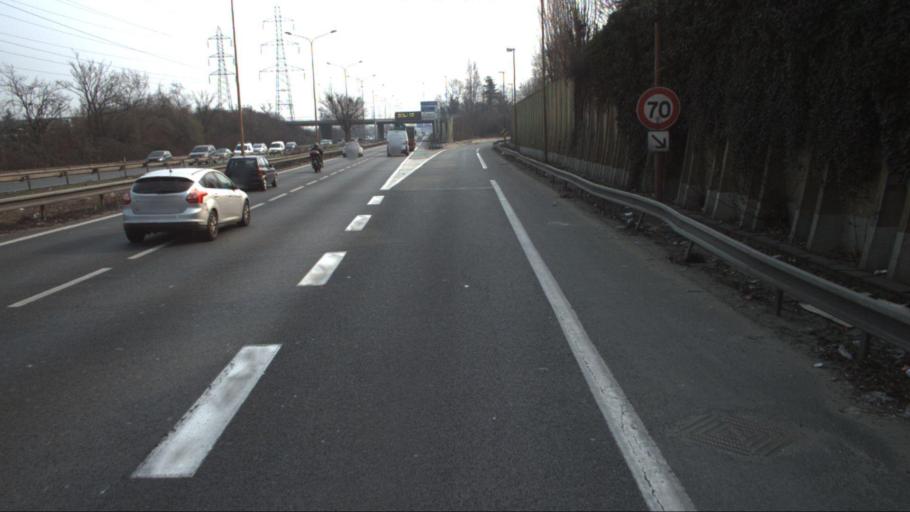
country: FR
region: Ile-de-France
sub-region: Departement des Hauts-de-Seine
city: Bois-Colombes
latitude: 48.9338
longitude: 2.2776
